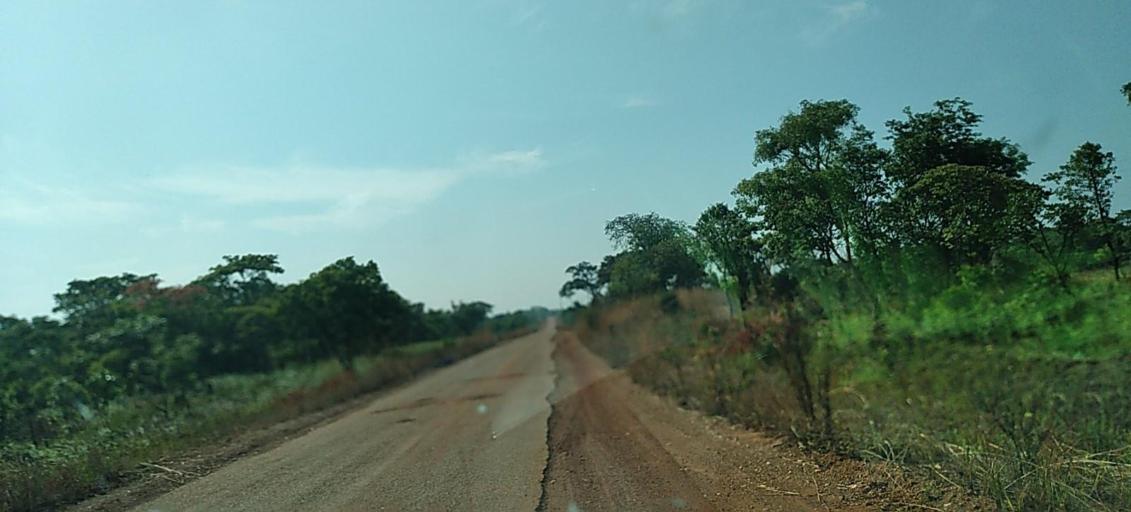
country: ZM
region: North-Western
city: Mwinilunga
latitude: -11.8142
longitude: 25.0887
